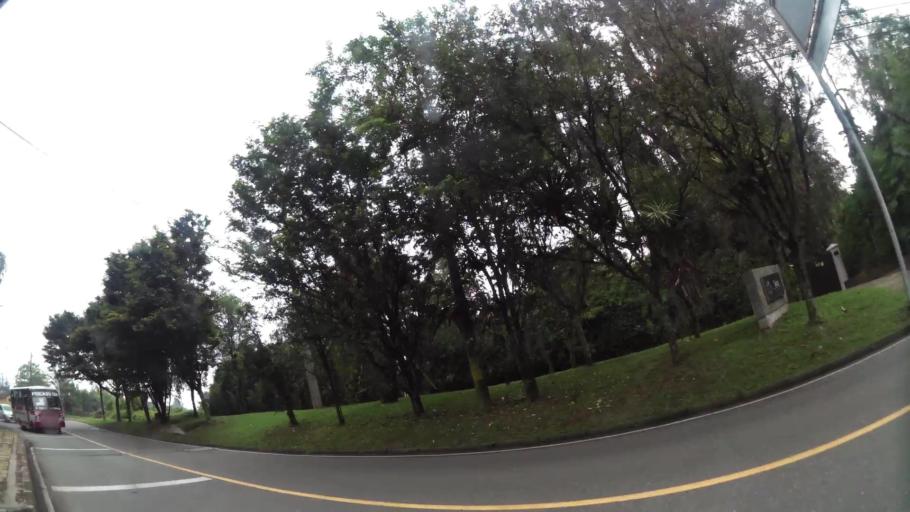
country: CO
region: Antioquia
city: Envigado
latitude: 6.1867
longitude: -75.5531
